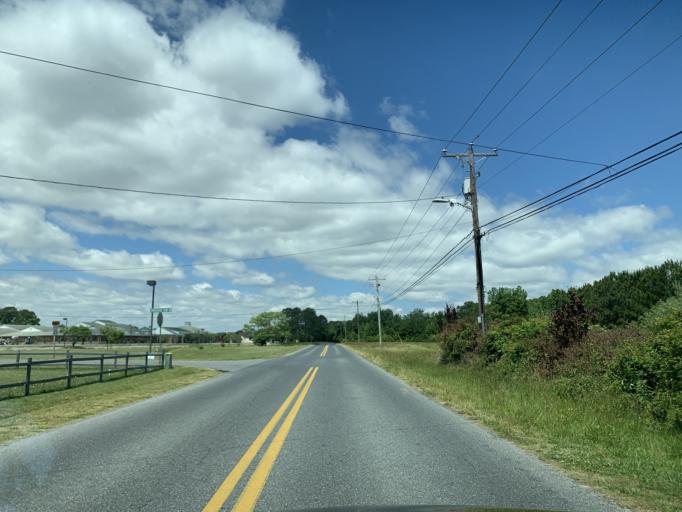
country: US
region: Maryland
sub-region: Worcester County
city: West Ocean City
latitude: 38.3468
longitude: -75.1039
